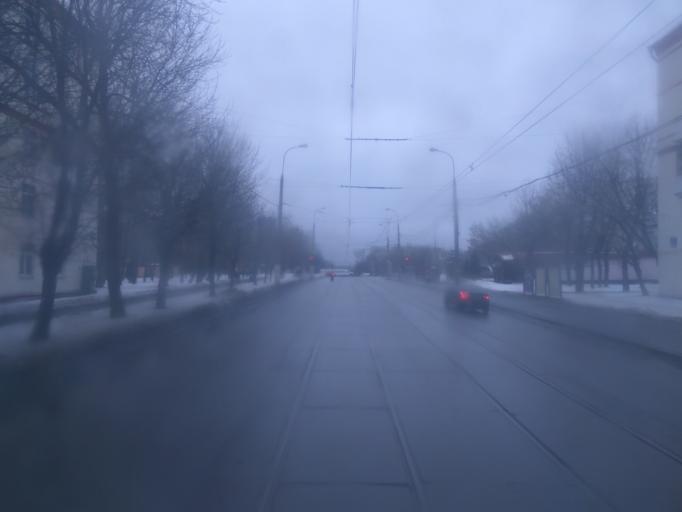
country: RU
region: Moskovskaya
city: Kozhukhovo
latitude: 55.6783
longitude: 37.6518
